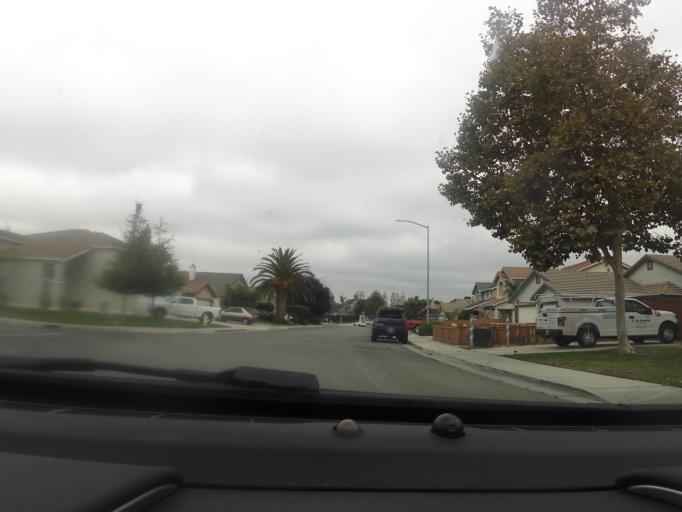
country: US
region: California
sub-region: San Benito County
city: Hollister
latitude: 36.8322
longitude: -121.3886
